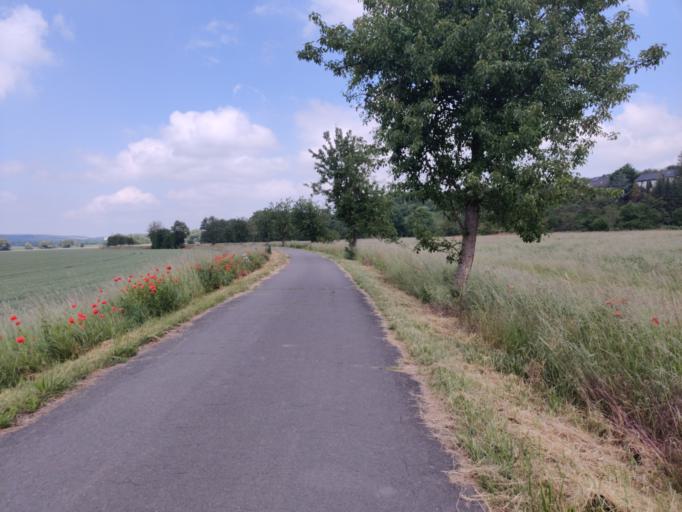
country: DE
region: Lower Saxony
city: Hildesheim
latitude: 52.1180
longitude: 9.9791
